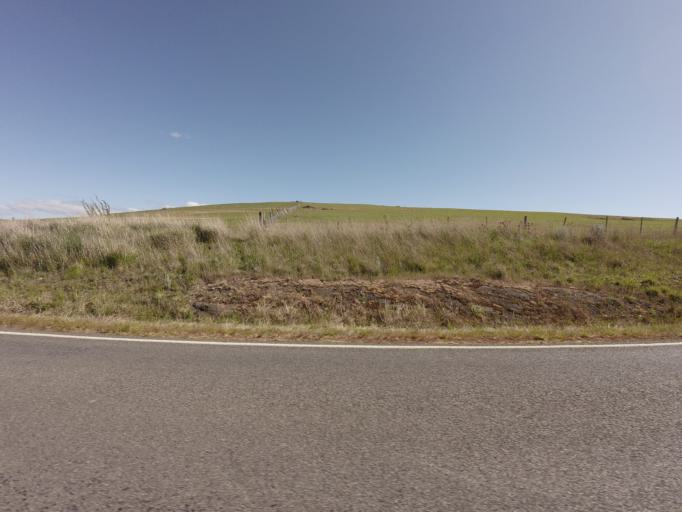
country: AU
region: Tasmania
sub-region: Derwent Valley
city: New Norfolk
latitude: -42.6457
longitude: 146.9236
